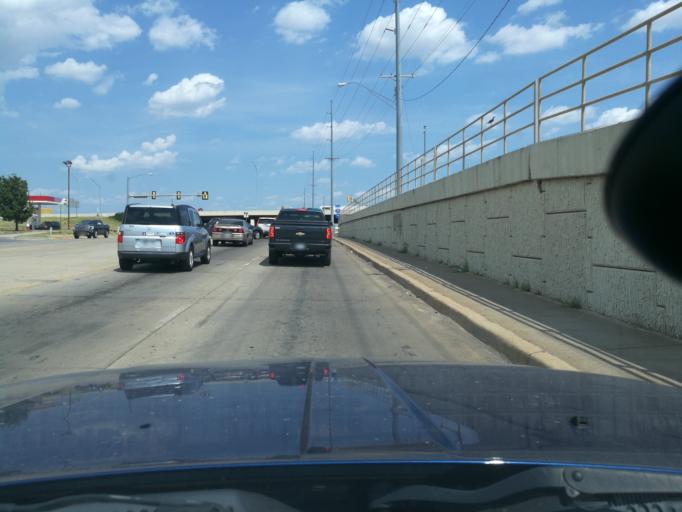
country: US
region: Oklahoma
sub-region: Oklahoma County
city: Del City
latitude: 35.4208
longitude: -97.4899
